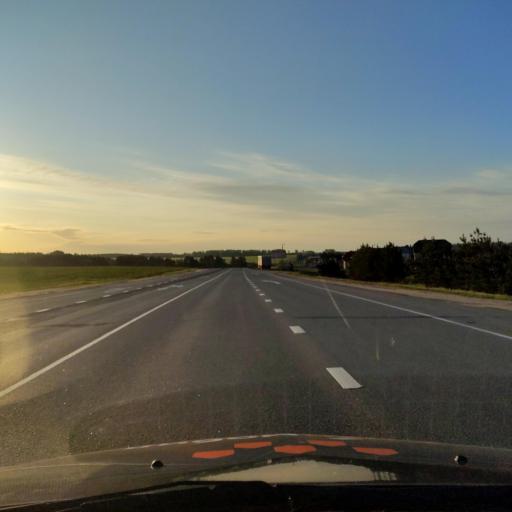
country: RU
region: Orjol
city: Livny
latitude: 52.4497
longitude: 37.5057
